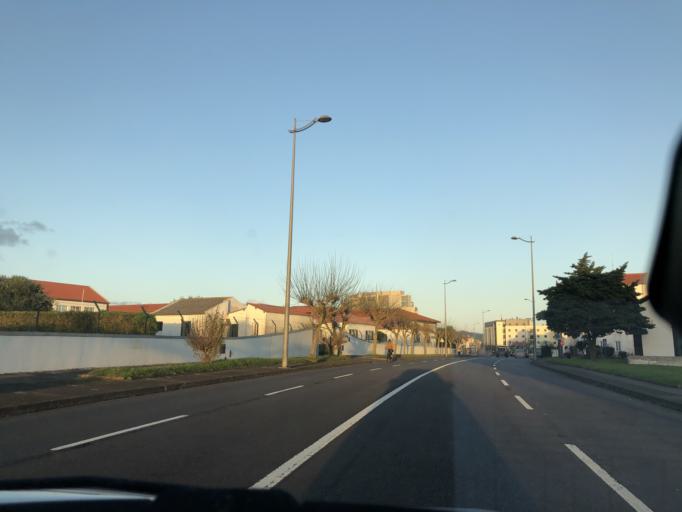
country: PT
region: Azores
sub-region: Ponta Delgada
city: Rosto de Cao
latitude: 37.7490
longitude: -25.6620
